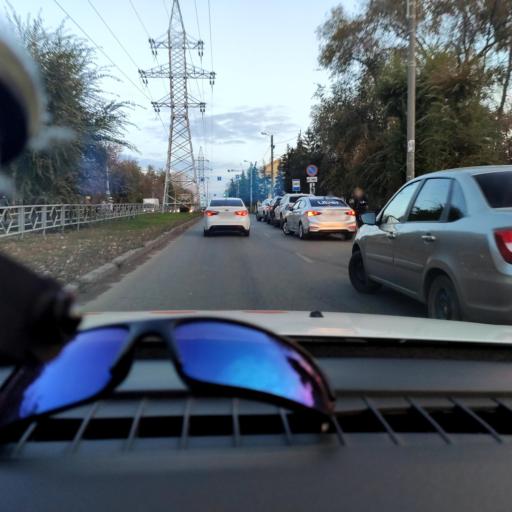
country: RU
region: Samara
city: Samara
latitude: 53.1995
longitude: 50.2142
